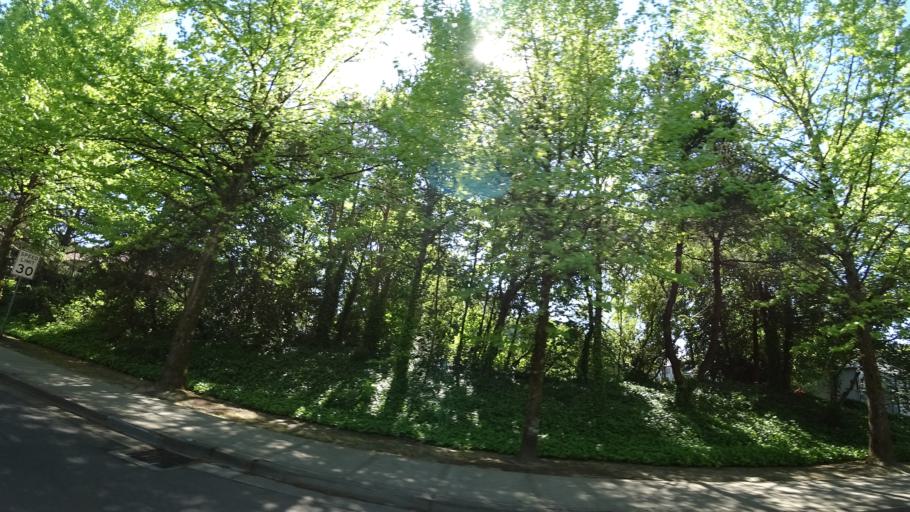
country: US
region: Oregon
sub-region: Washington County
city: Beaverton
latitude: 45.4523
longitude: -122.8030
